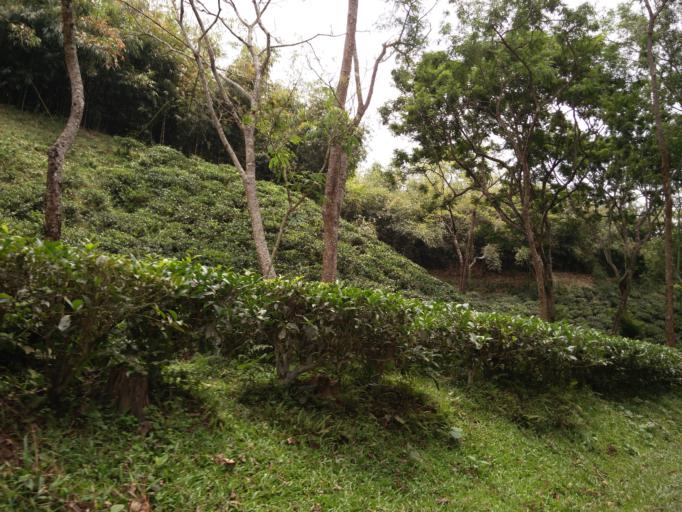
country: IN
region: Tripura
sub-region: Dhalai
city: Kamalpur
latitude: 24.3061
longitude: 91.8018
